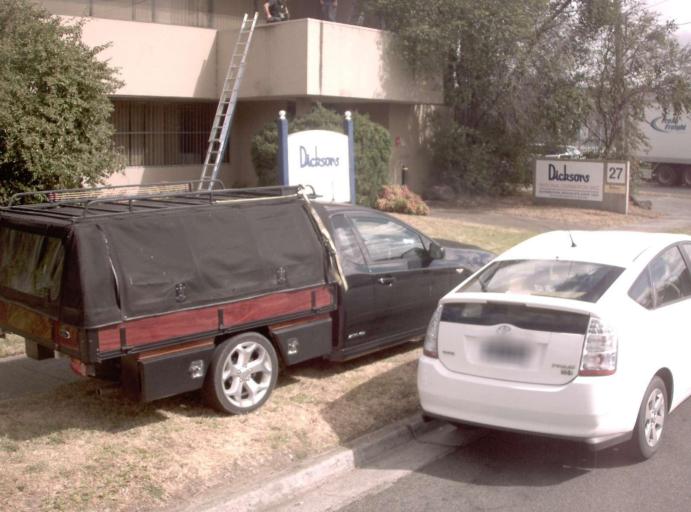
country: AU
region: Victoria
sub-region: Monash
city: Oakleigh South
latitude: -37.9299
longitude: 145.1000
